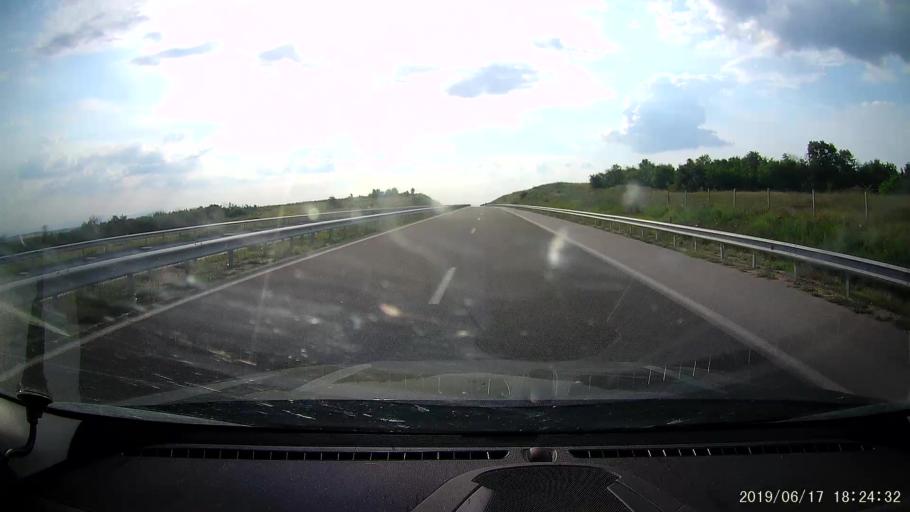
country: BG
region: Khaskovo
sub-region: Obshtina Dimitrovgrad
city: Dimitrovgrad
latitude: 41.9854
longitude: 25.6890
